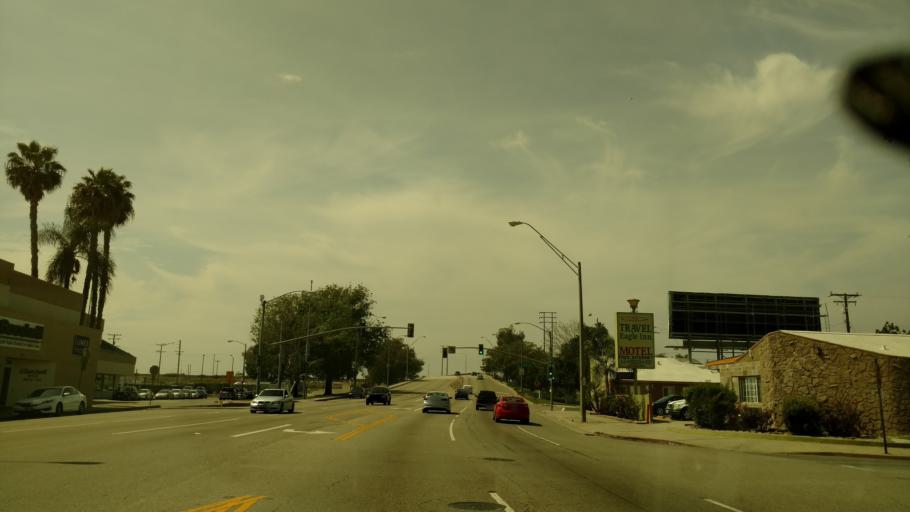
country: US
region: California
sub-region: Los Angeles County
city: Long Beach
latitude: 33.7899
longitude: -118.2016
